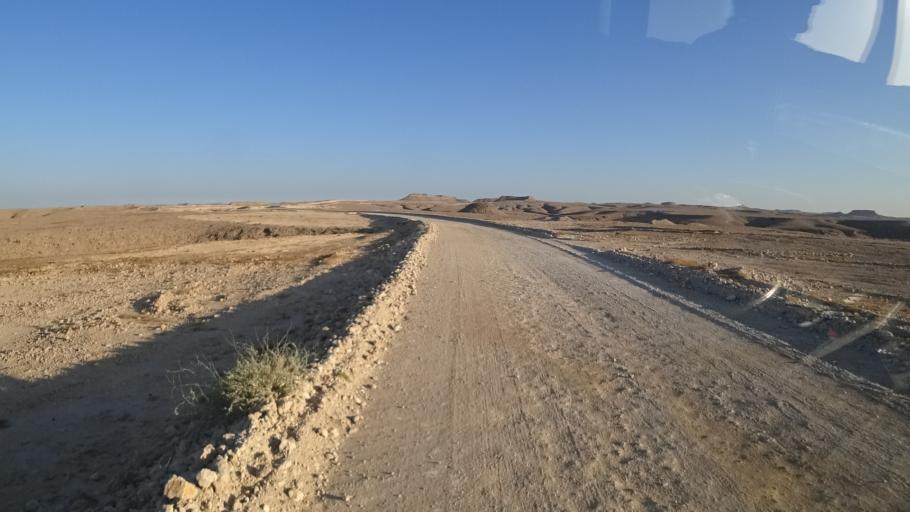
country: YE
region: Al Mahrah
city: Hawf
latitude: 17.1550
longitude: 53.3505
